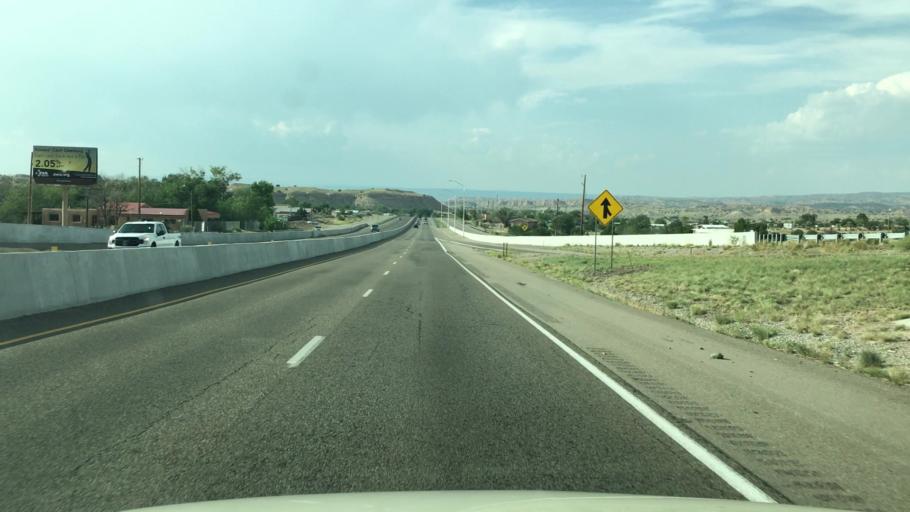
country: US
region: New Mexico
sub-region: Santa Fe County
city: El Valle de Arroyo Seco
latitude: 35.9307
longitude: -106.0180
